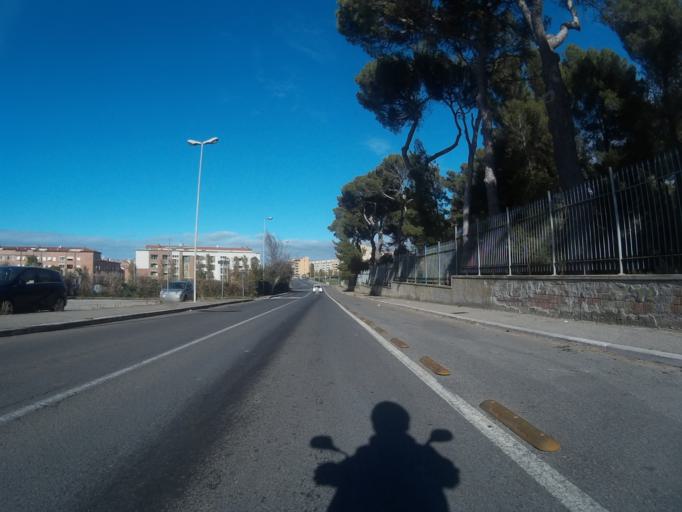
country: IT
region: Tuscany
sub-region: Provincia di Livorno
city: Livorno
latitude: 43.5236
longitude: 10.3463
